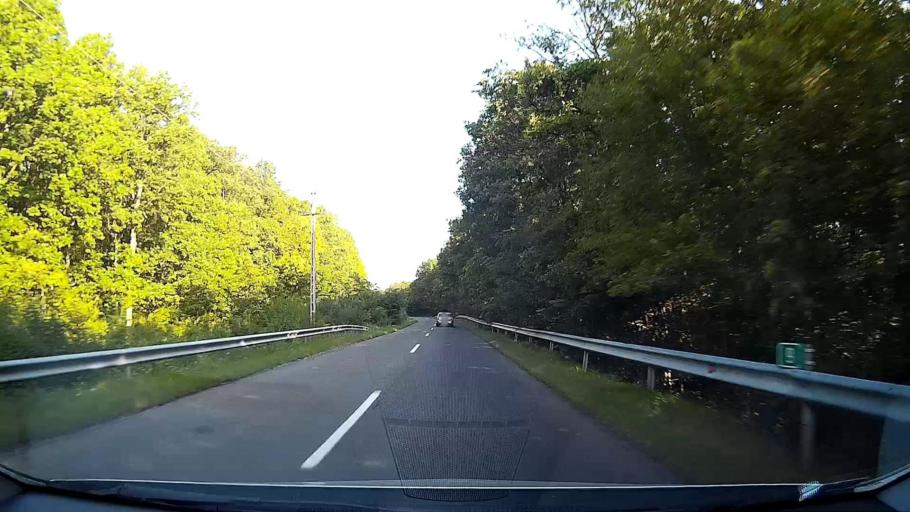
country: HU
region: Pest
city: Nagykovacsi
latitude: 47.7162
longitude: 19.0119
